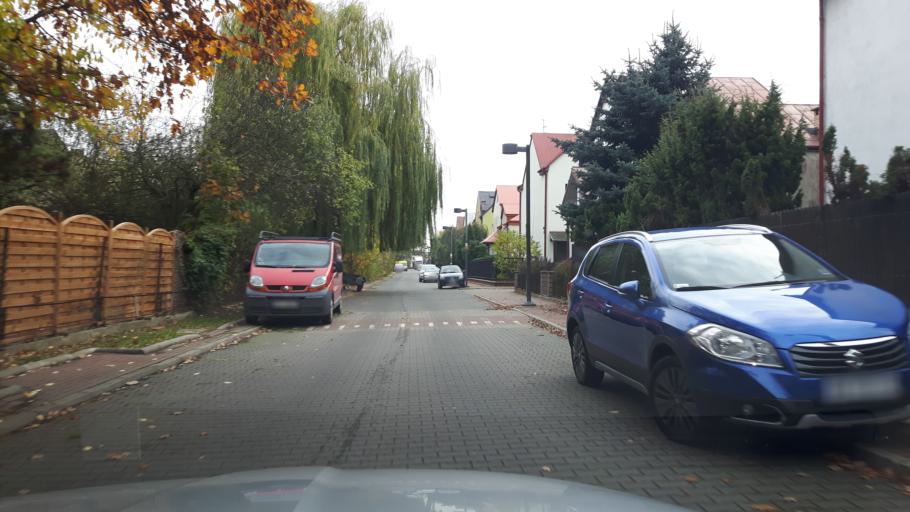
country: PL
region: Masovian Voivodeship
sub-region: Warszawa
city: Targowek
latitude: 52.2866
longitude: 21.0571
